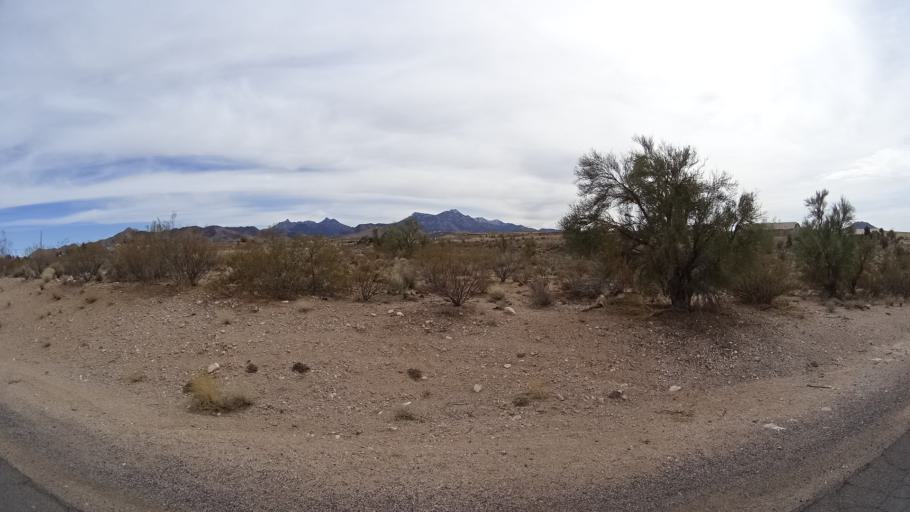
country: US
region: Arizona
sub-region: Mohave County
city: Kingman
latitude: 35.1807
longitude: -113.9983
